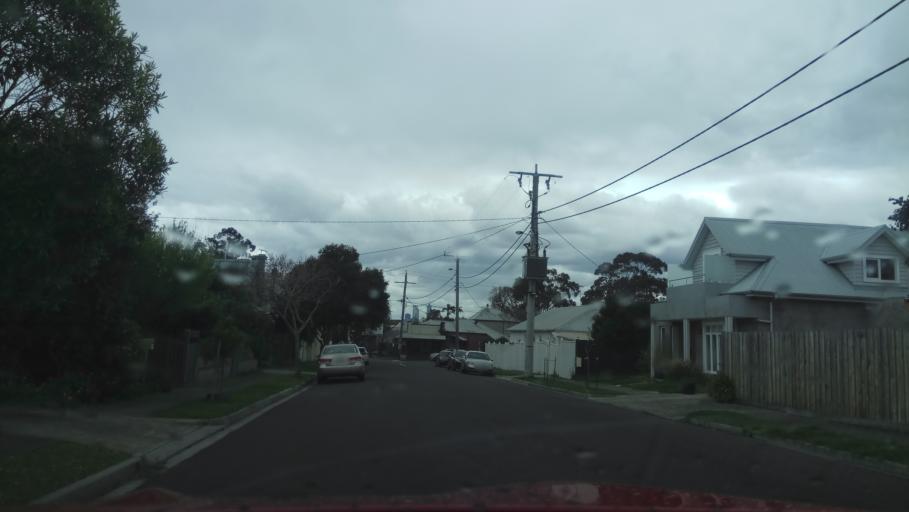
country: AU
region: Victoria
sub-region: Hobsons Bay
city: Newport
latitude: -37.8491
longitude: 144.8923
